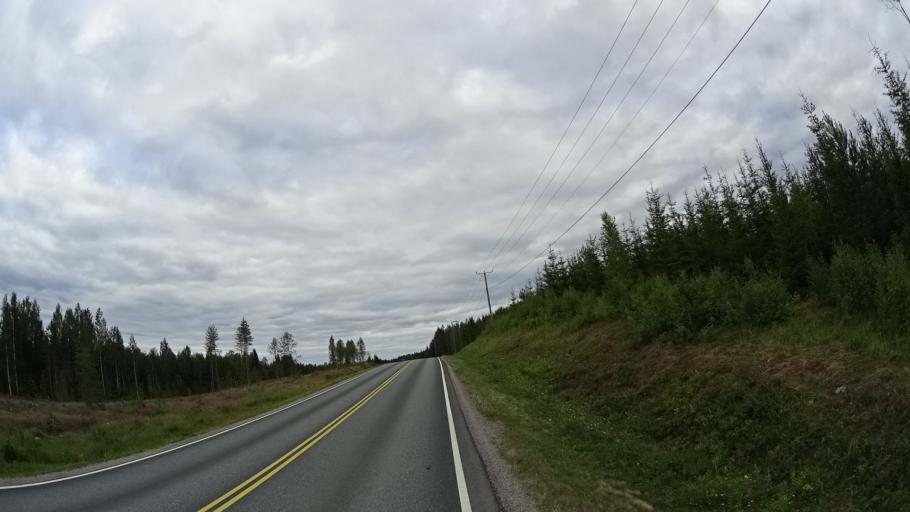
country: FI
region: Satakunta
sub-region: Pohjois-Satakunta
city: Jaemijaervi
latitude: 61.7780
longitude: 22.8641
